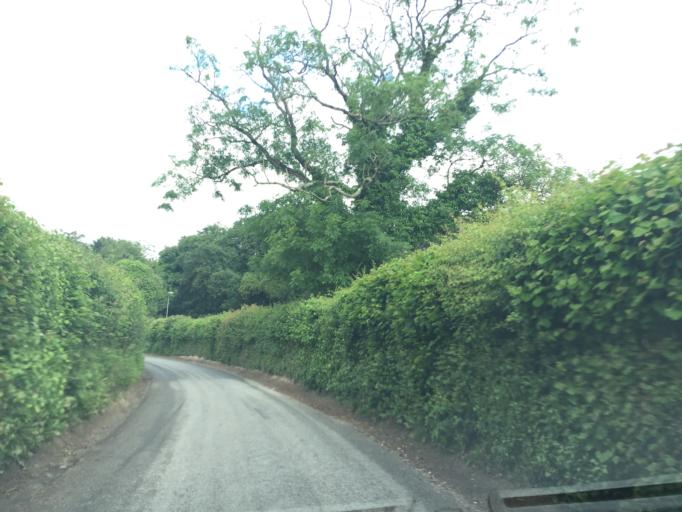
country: GB
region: England
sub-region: Dorset
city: Dorchester
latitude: 50.7461
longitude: -2.3402
